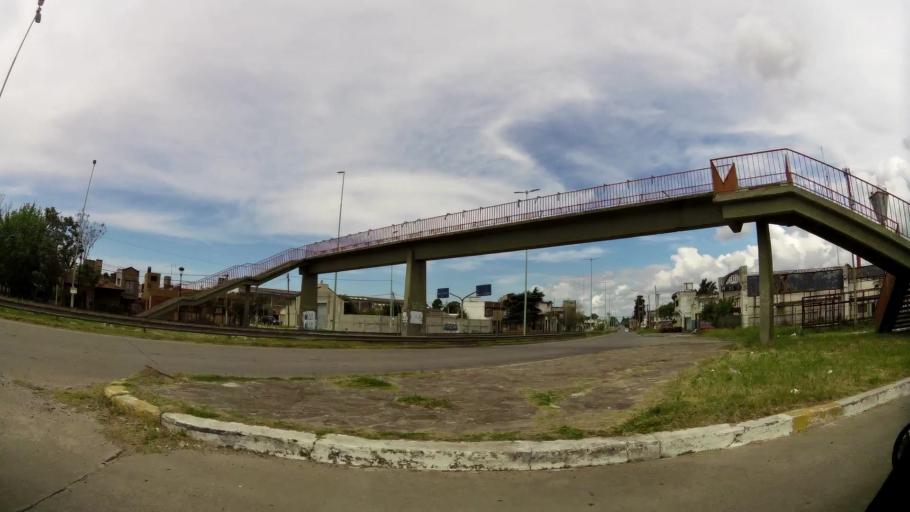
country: AR
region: Buenos Aires
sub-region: Partido de Quilmes
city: Quilmes
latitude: -34.7831
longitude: -58.2585
